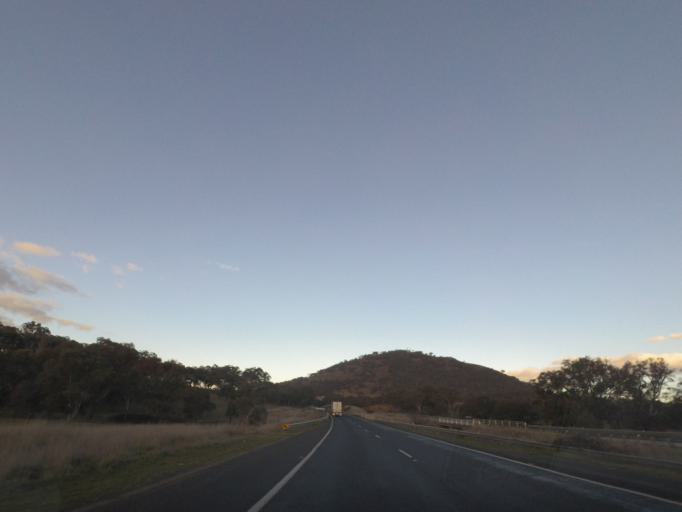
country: AU
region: New South Wales
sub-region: Yass Valley
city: Yass
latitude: -34.7732
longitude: 148.8147
